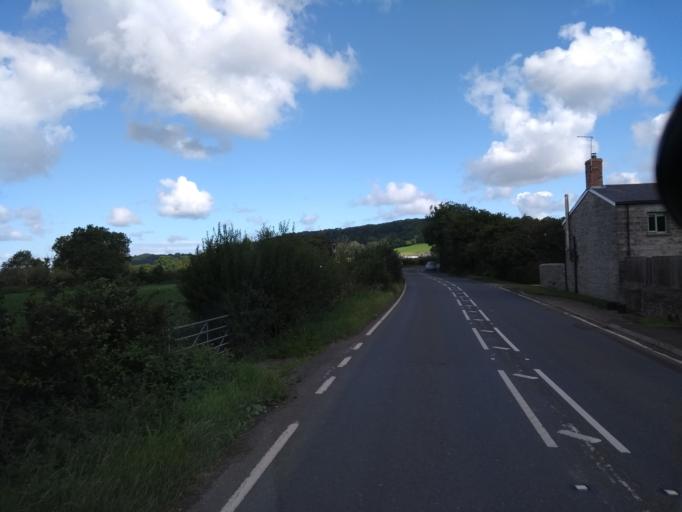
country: GB
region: England
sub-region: Somerset
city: Street
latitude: 51.0984
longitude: -2.7354
